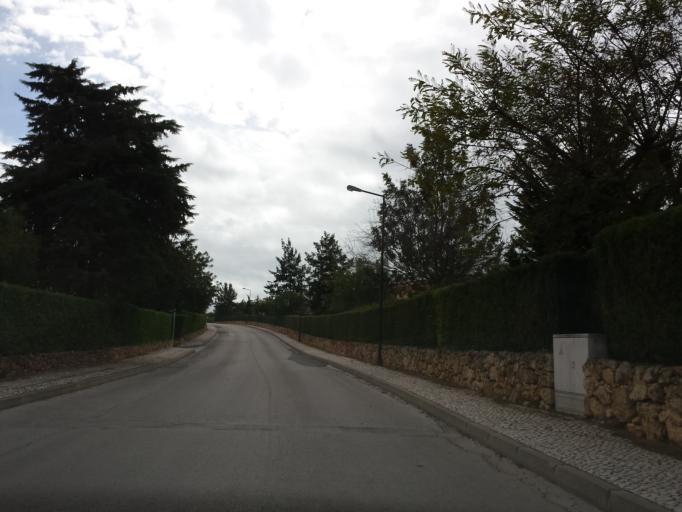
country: PT
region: Faro
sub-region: Lagoa
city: Estombar
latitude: 37.1282
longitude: -8.4857
